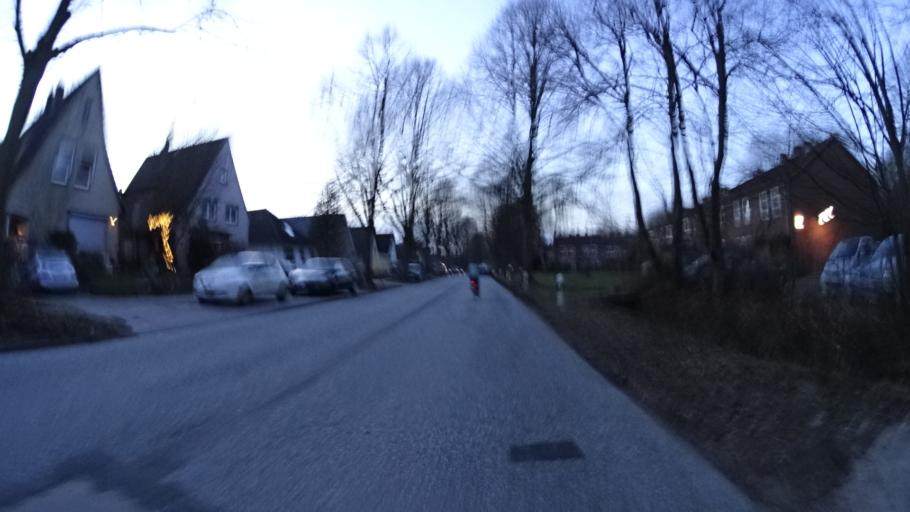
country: DE
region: Hamburg
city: Stellingen
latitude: 53.6016
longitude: 9.9312
